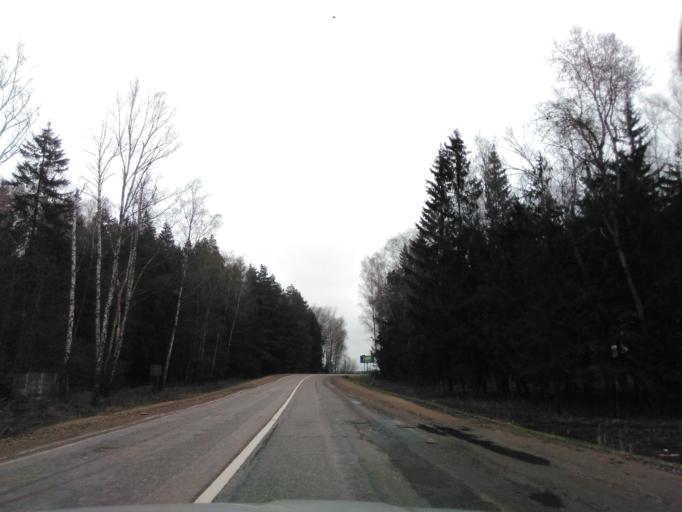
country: RU
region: Moskovskaya
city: Rozhdestveno
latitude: 55.8320
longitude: 37.0261
